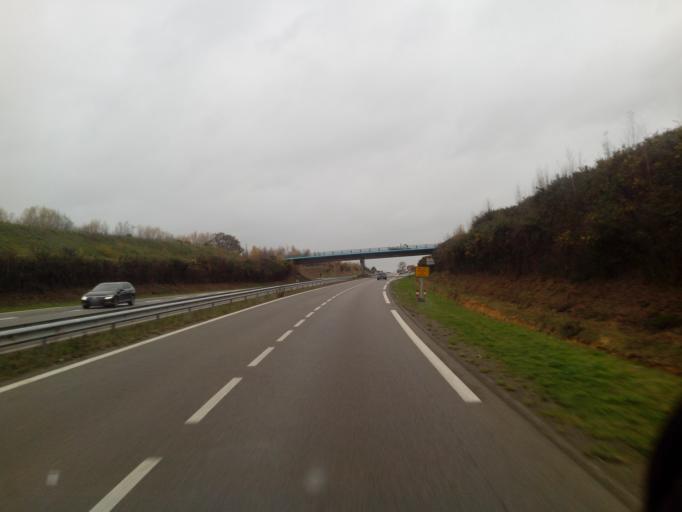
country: FR
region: Brittany
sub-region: Departement d'Ille-et-Vilaine
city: Chevaigne
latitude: 48.2074
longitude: -1.6233
